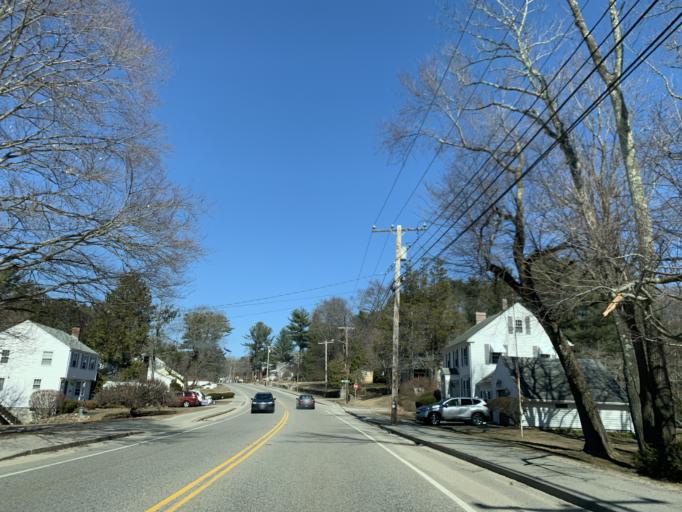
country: US
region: Massachusetts
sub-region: Norfolk County
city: Sharon
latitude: 42.1148
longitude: -71.1850
